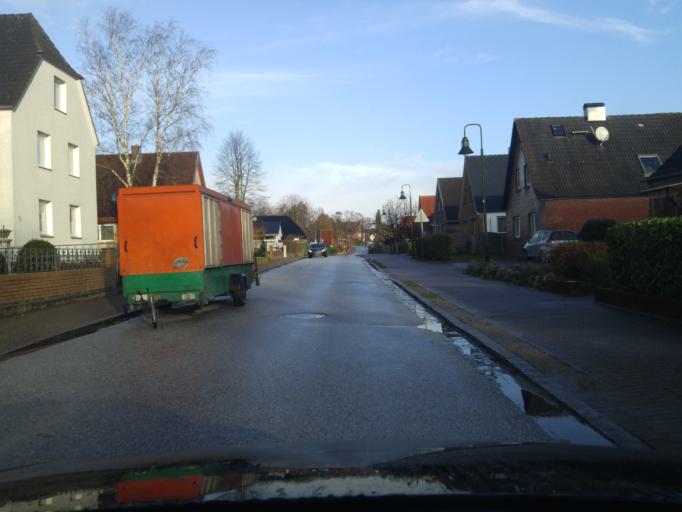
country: DE
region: Schleswig-Holstein
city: Ratekau
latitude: 53.9422
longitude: 10.7330
